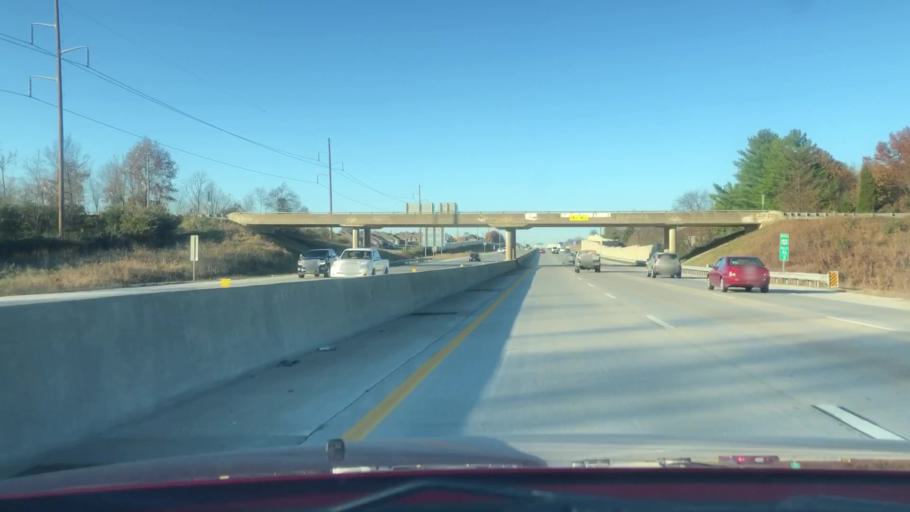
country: US
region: Missouri
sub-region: Greene County
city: Springfield
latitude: 37.1444
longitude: -93.2247
